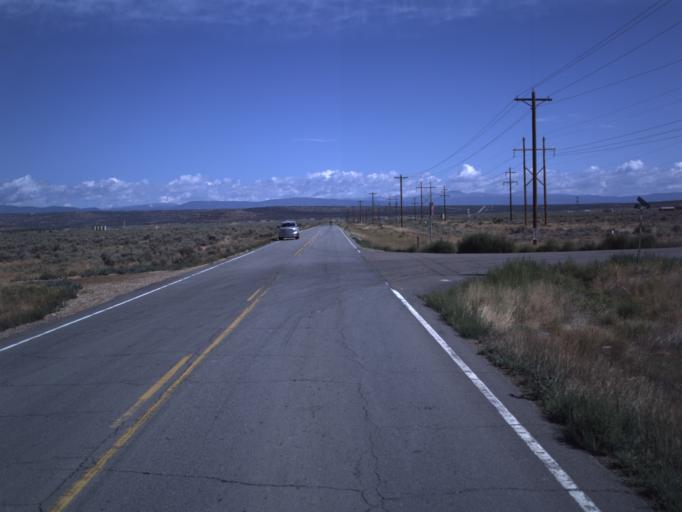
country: US
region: Utah
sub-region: Duchesne County
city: Duchesne
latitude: 40.2272
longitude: -110.3893
